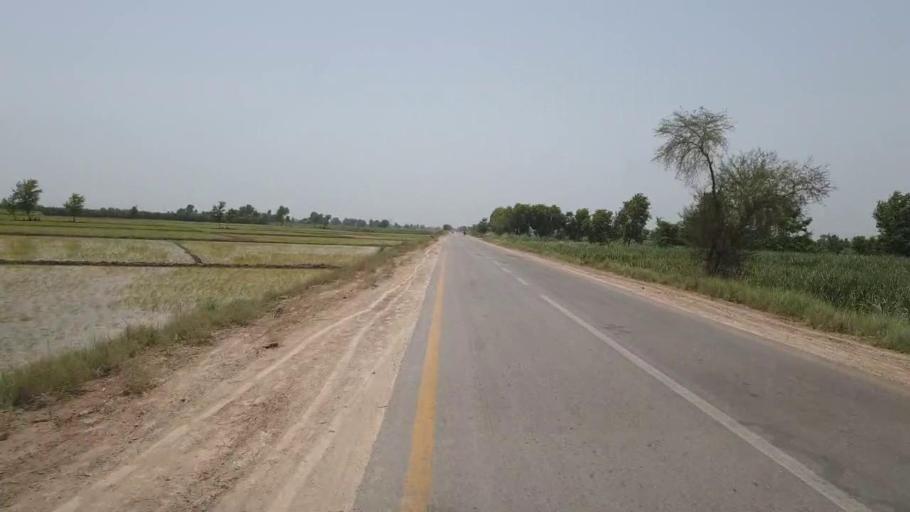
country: PK
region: Sindh
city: Moro
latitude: 26.6032
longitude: 68.0570
